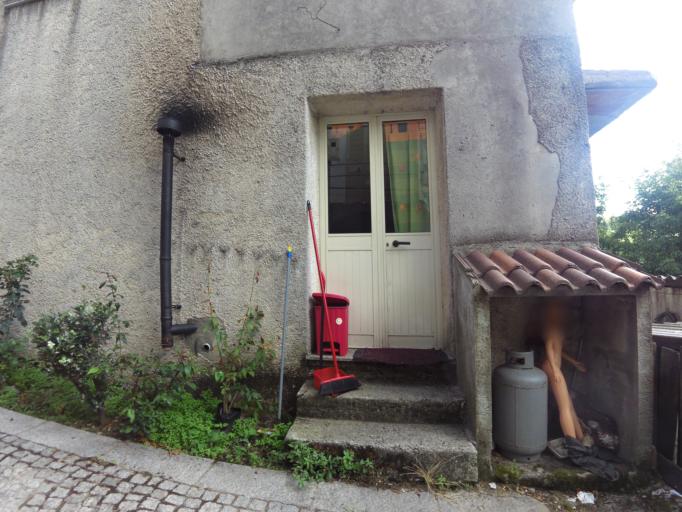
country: IT
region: Calabria
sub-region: Provincia di Vibo-Valentia
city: Mongiana
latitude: 38.5120
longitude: 16.3197
